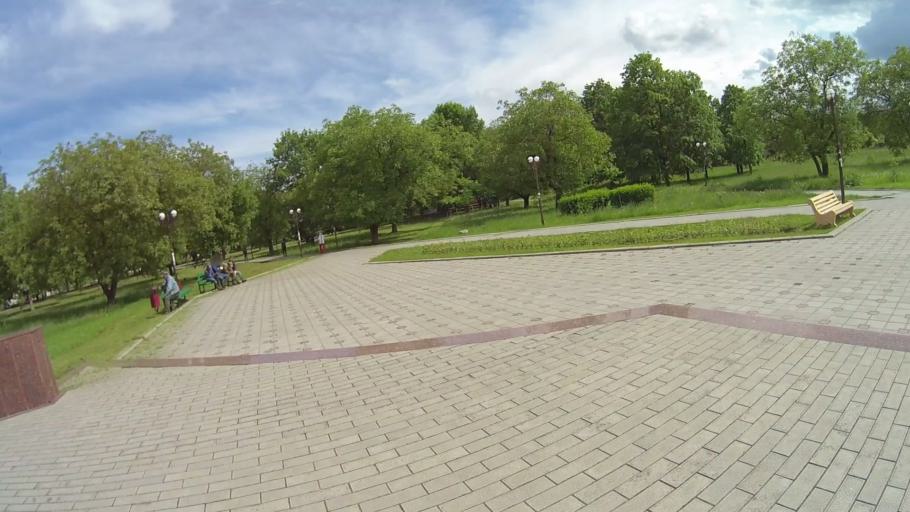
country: RU
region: Kabardino-Balkariya
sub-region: Gorod Nal'chik
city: Nal'chik
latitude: 43.4772
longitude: 43.5880
